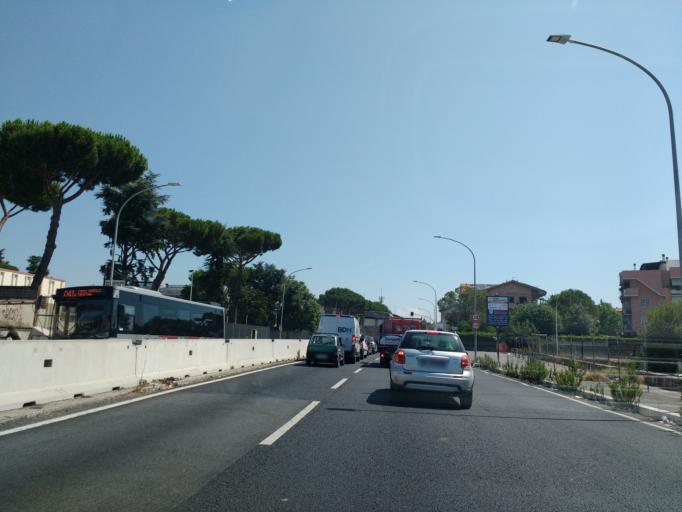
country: IT
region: Latium
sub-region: Citta metropolitana di Roma Capitale
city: Setteville
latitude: 41.9372
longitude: 12.6181
